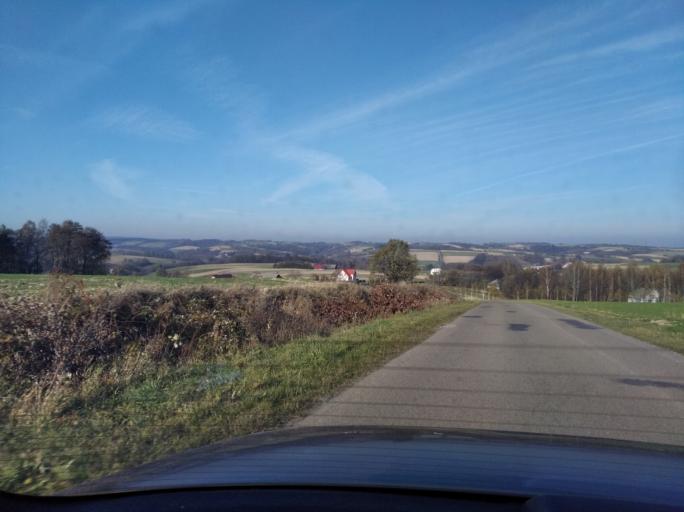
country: PL
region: Subcarpathian Voivodeship
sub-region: Powiat ropczycko-sedziszowski
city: Wielopole Skrzynskie
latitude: 49.9177
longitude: 21.5650
